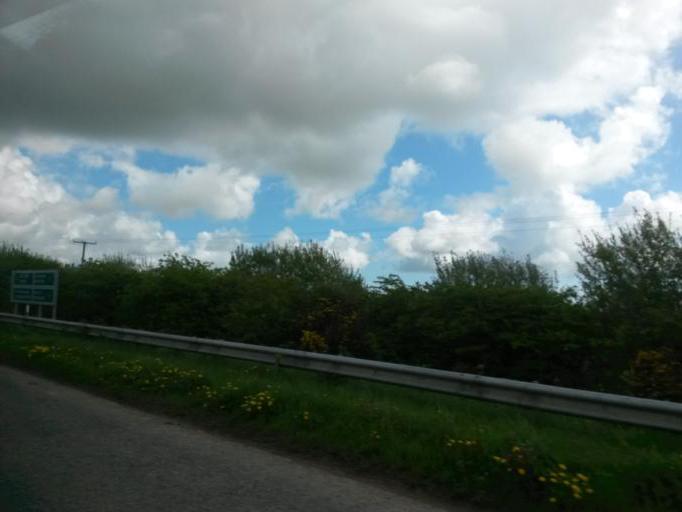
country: IE
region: Leinster
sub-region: Loch Garman
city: Castlebridge
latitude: 52.3988
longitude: -6.5195
